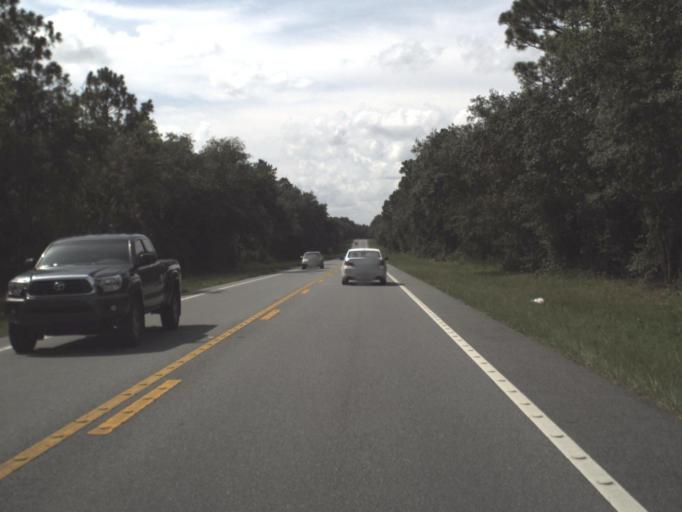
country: US
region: Florida
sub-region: Citrus County
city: Citrus Springs
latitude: 28.9843
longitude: -82.4332
